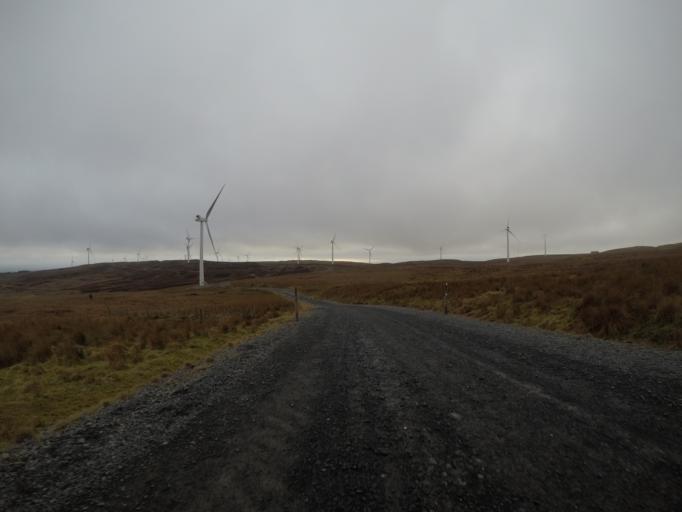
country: GB
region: Scotland
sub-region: North Ayrshire
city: Fairlie
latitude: 55.7576
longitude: -4.7953
